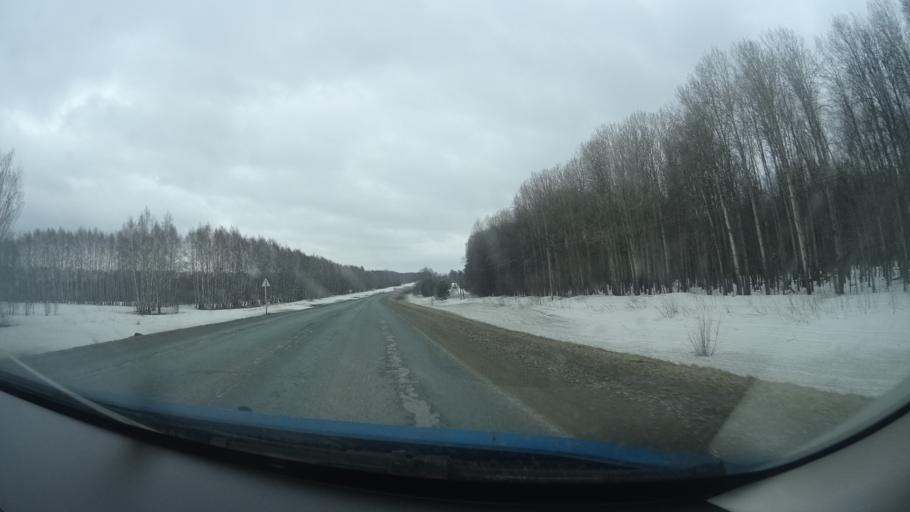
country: RU
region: Bashkortostan
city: Birsk
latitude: 55.3142
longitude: 55.6253
